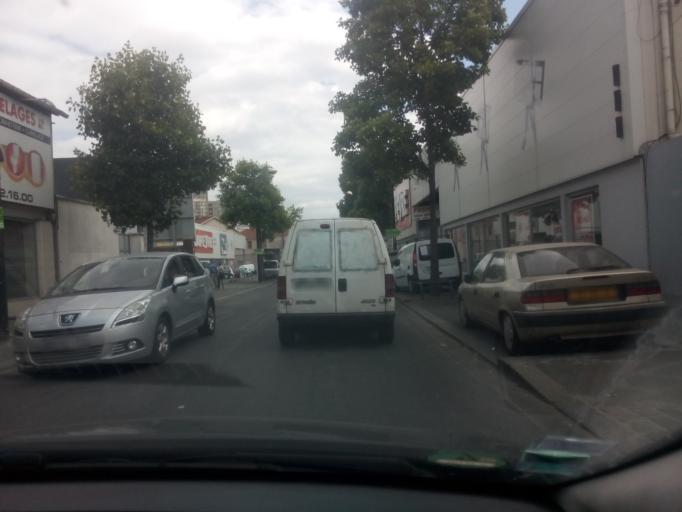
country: FR
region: Ile-de-France
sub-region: Departement de Seine-Saint-Denis
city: Aubervilliers
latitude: 48.9051
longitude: 2.3814
